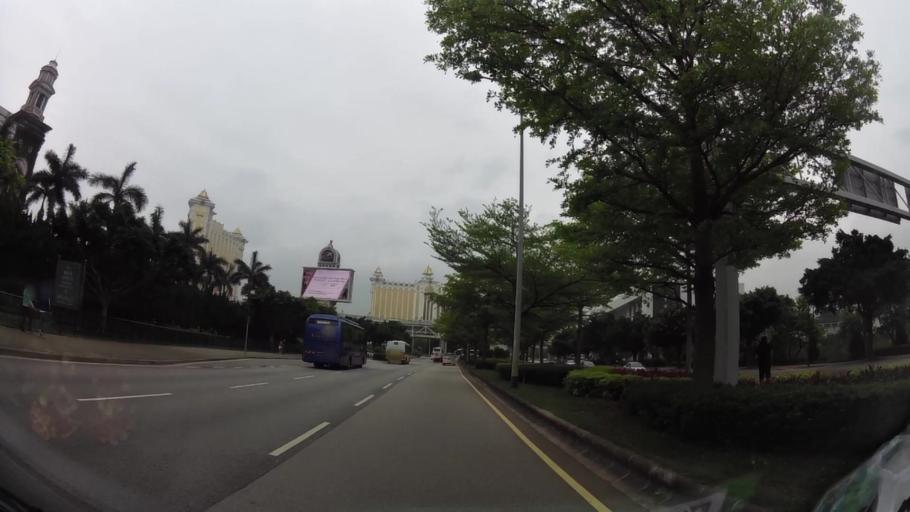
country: MO
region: Macau
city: Macau
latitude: 22.1499
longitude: 113.5597
